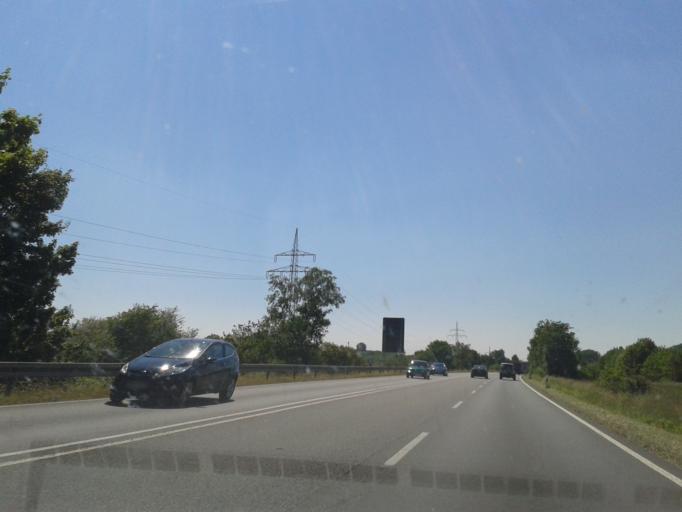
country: DE
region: North Rhine-Westphalia
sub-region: Regierungsbezirk Detmold
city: Paderborn
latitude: 51.7560
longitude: 8.7594
